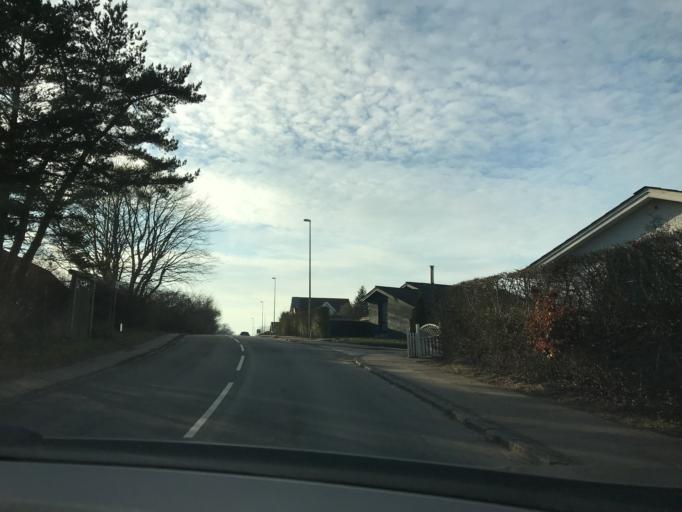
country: DK
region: South Denmark
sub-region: Vejle Kommune
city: Vejle
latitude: 55.7154
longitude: 9.5639
